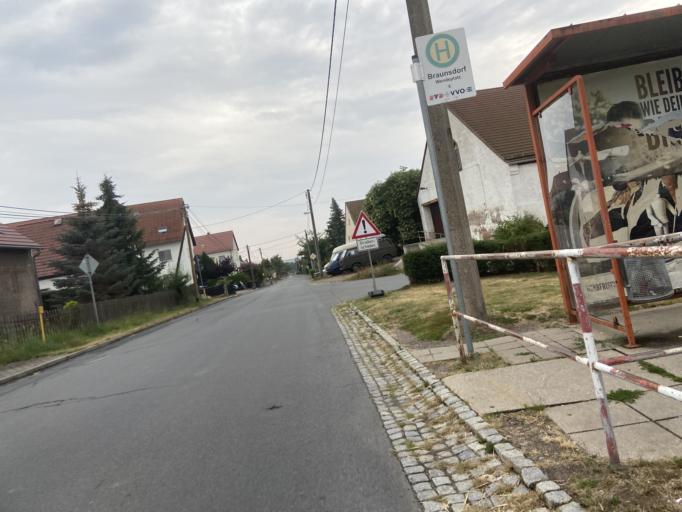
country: DE
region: Saxony
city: Tharandt
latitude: 51.0161
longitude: 13.5717
